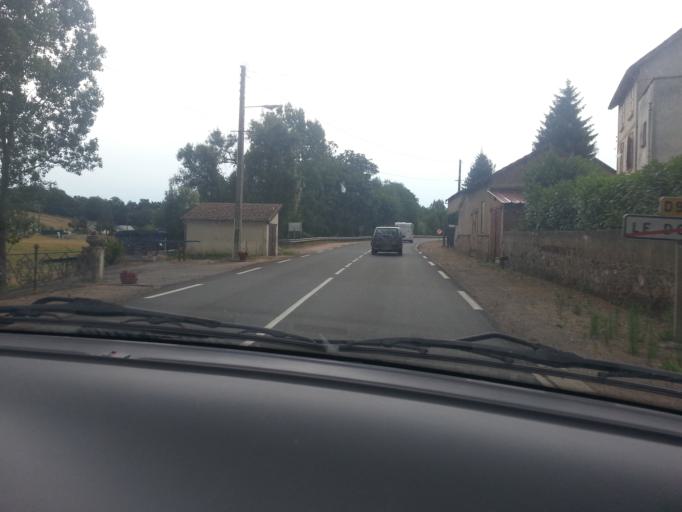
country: FR
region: Auvergne
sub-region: Departement de l'Allier
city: Le Donjon
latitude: 46.3505
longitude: 3.7994
